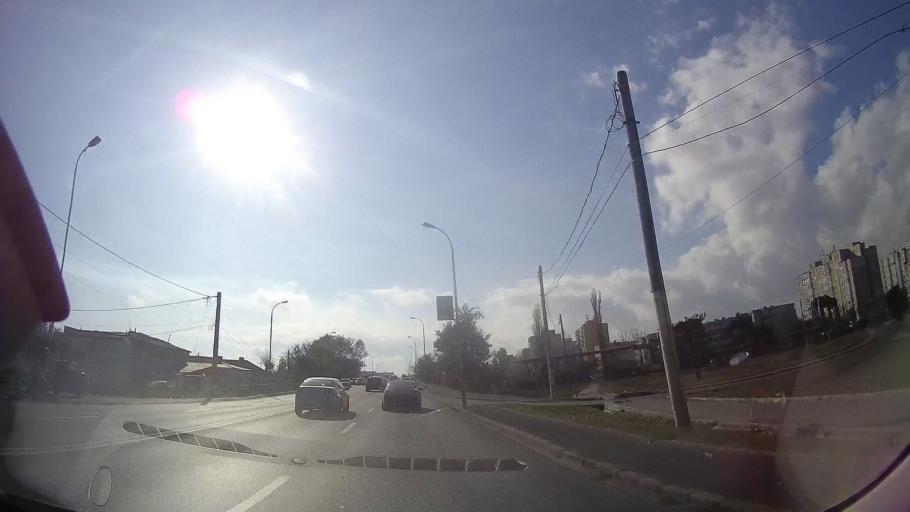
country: RO
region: Constanta
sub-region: Municipiul Constanta
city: Constanta
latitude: 44.1508
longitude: 28.6270
